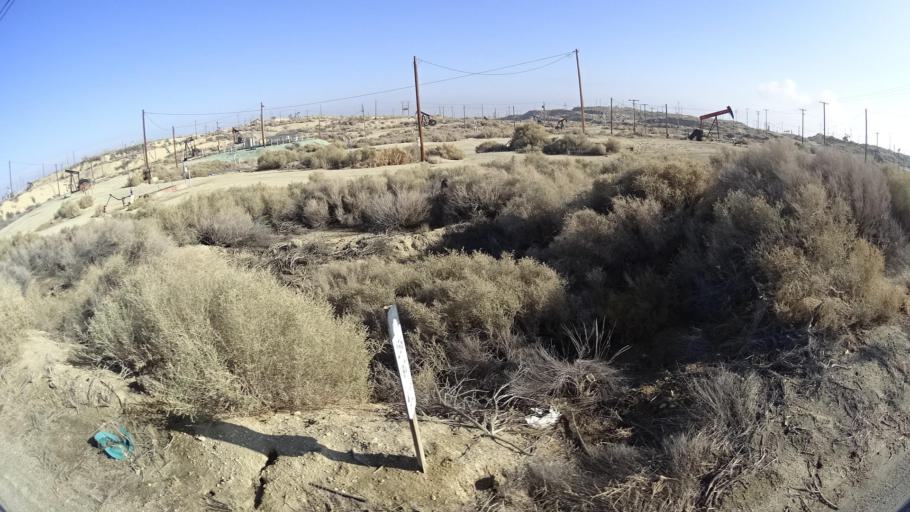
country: US
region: California
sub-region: Kern County
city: Taft Heights
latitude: 35.2196
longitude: -119.6093
